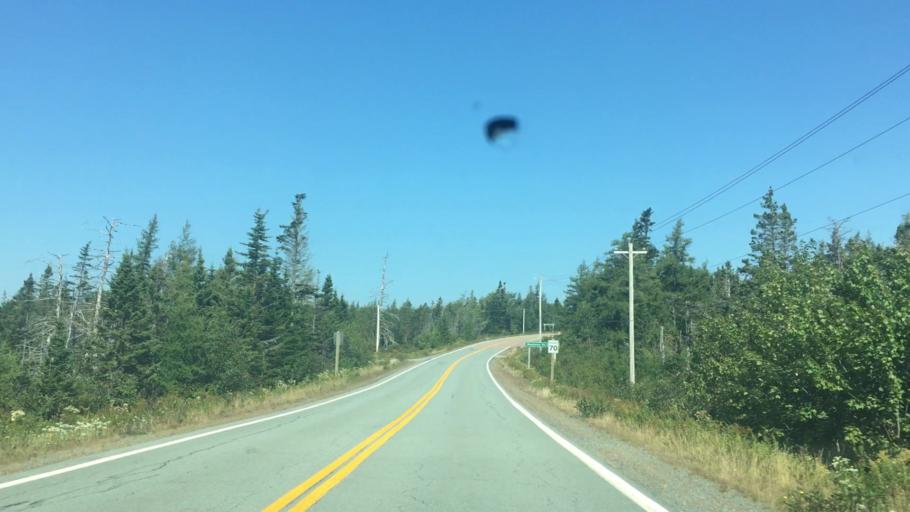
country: CA
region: Nova Scotia
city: Antigonish
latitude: 45.0228
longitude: -62.0313
